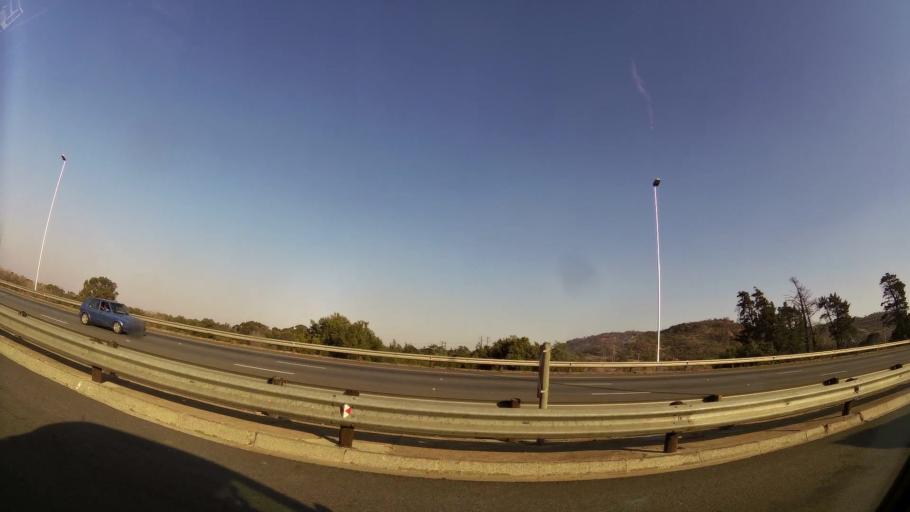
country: ZA
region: Gauteng
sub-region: Ekurhuleni Metropolitan Municipality
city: Germiston
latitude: -26.2633
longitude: 28.1002
